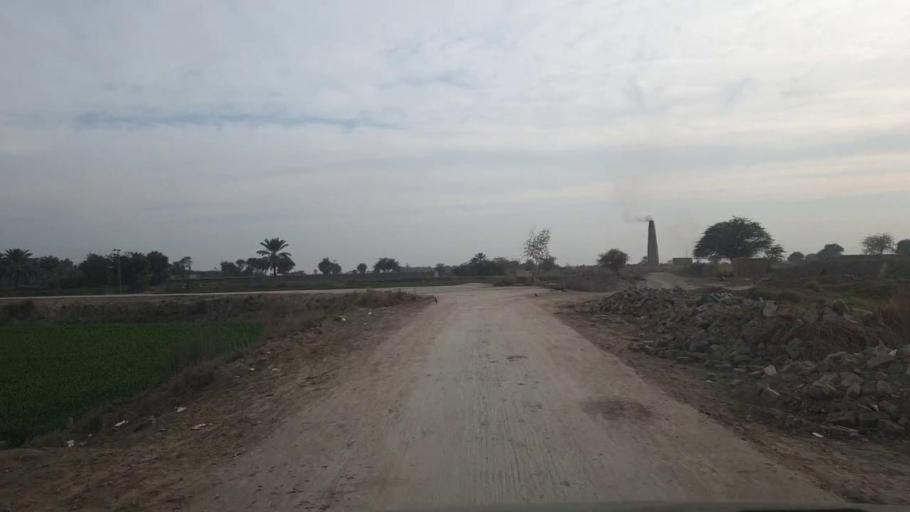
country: PK
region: Sindh
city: Shahpur Chakar
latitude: 26.1353
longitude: 68.6051
